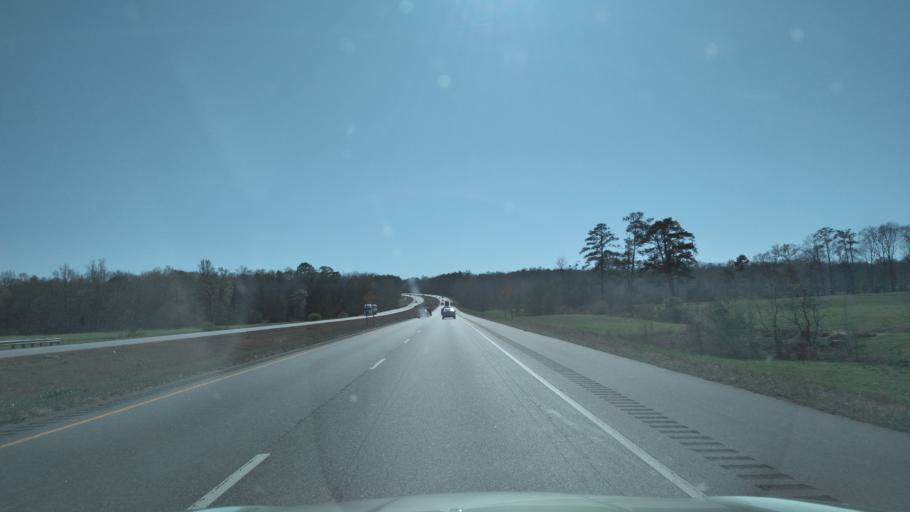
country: US
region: Alabama
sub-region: Lowndes County
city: Fort Deposit
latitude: 31.9486
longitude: -86.5556
